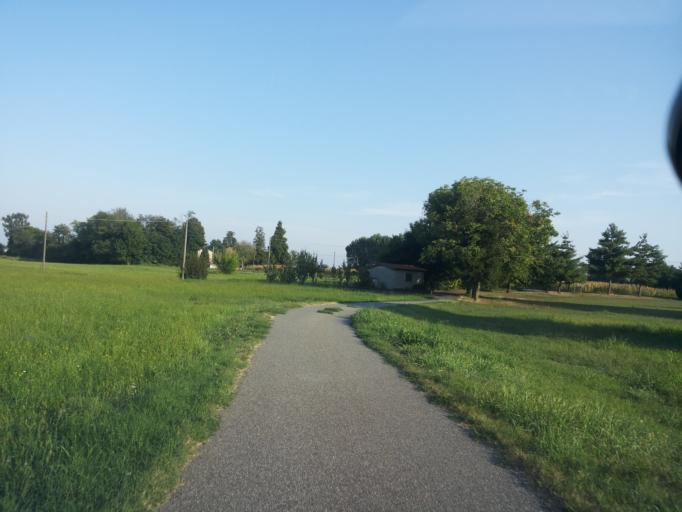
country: IT
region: Piedmont
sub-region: Provincia di Biella
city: Cavaglia
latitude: 45.3955
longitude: 8.1103
